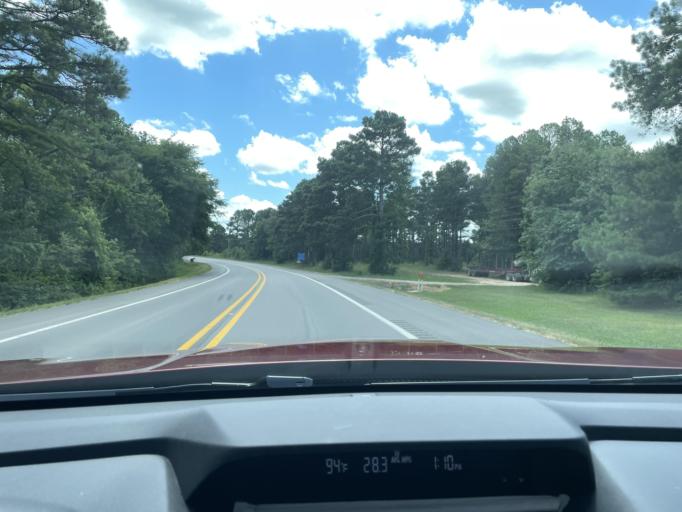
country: US
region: Arkansas
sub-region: Drew County
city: Monticello
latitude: 33.7154
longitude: -91.8113
